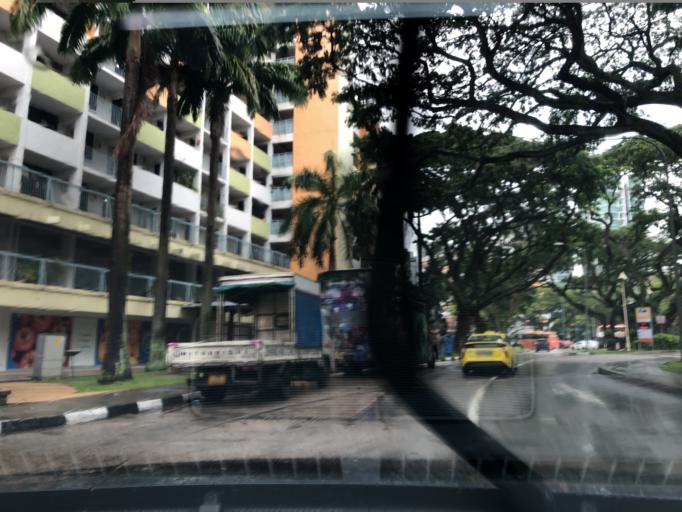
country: SG
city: Singapore
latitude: 1.2897
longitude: 103.8274
